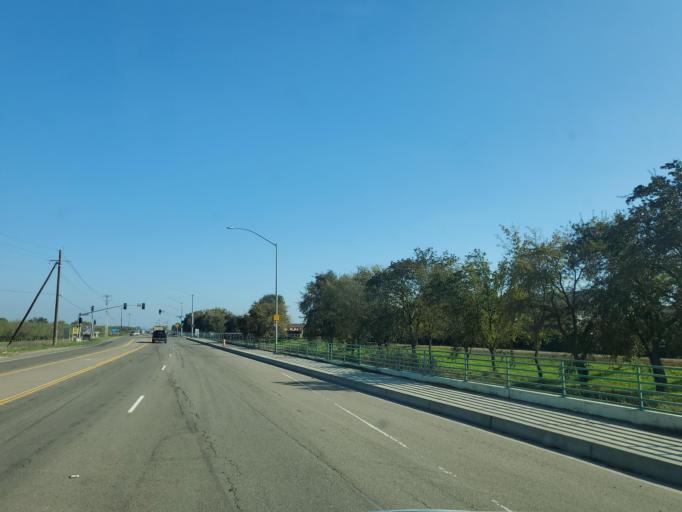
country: US
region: California
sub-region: San Joaquin County
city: Lincoln Village
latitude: 38.0576
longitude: -121.3193
